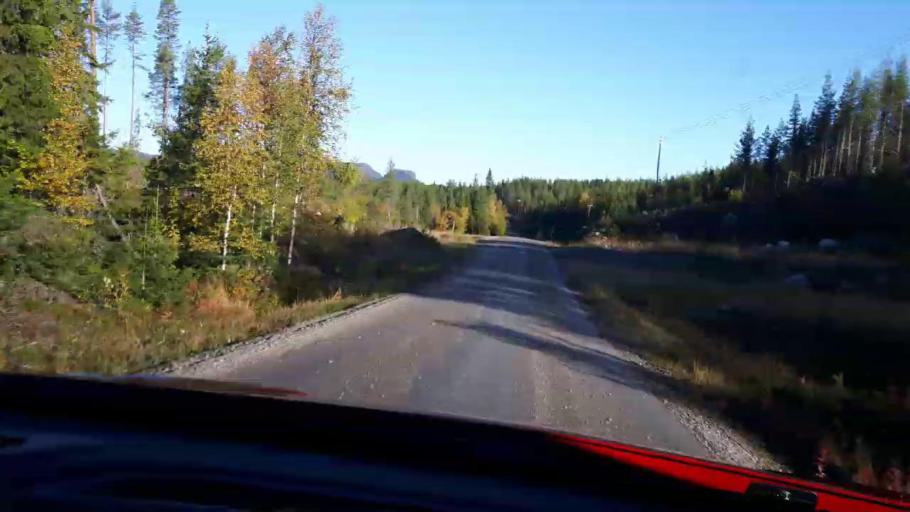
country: SE
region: Jaemtland
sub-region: Stroemsunds Kommun
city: Stroemsund
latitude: 64.3700
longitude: 15.1577
